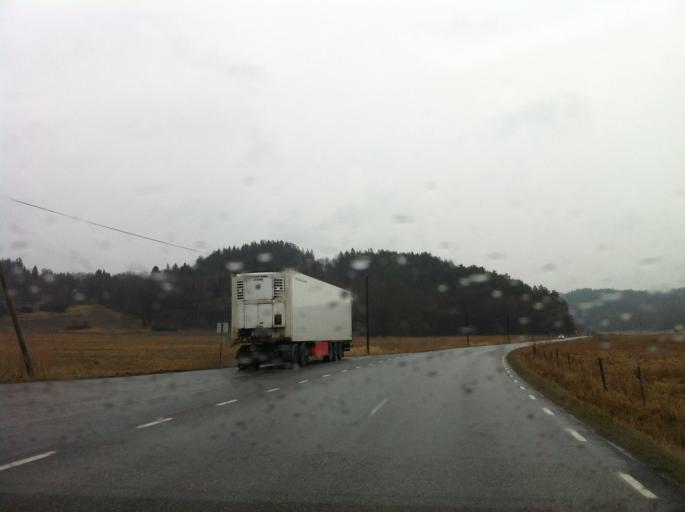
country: SE
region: Vaestra Goetaland
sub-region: Lysekils Kommun
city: Brastad
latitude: 58.4579
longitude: 11.4516
